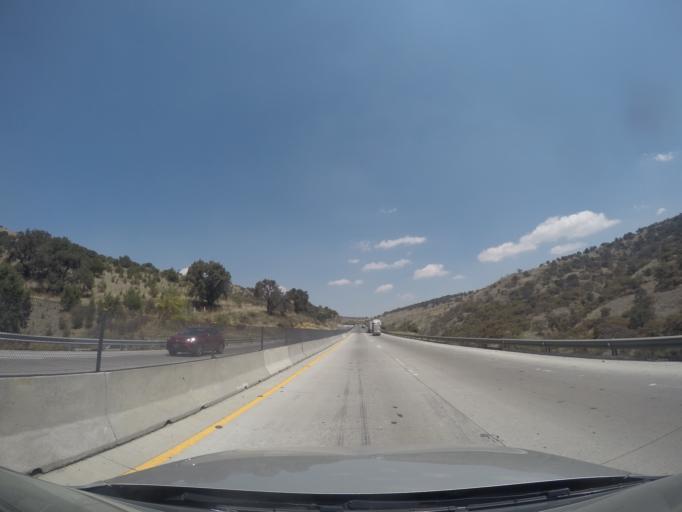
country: MX
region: Puebla
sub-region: San Matias Tlalancaleca
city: San Francisco Tlaloc
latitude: 19.3908
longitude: -98.4196
